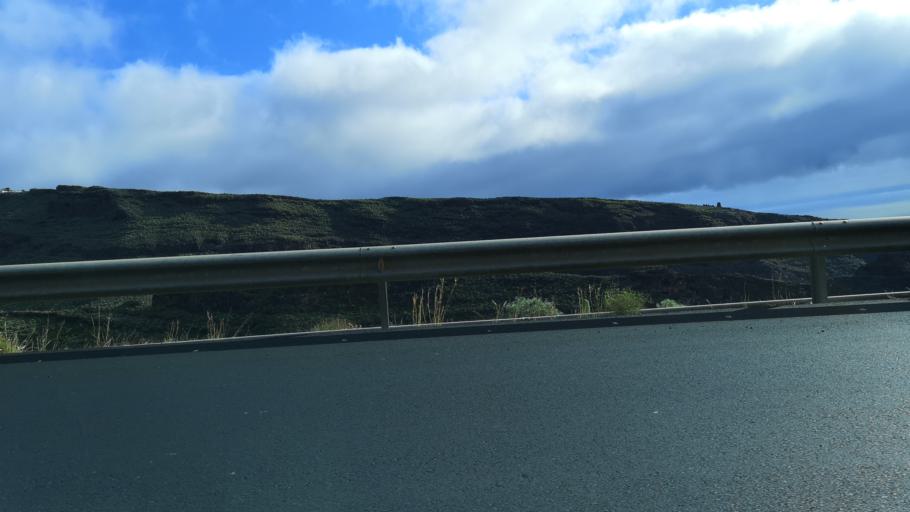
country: ES
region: Canary Islands
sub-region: Provincia de Santa Cruz de Tenerife
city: Alajero
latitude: 28.0612
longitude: -17.2027
